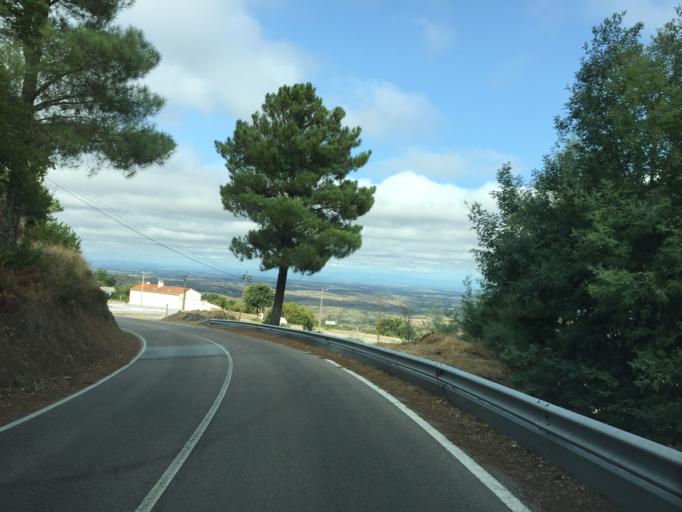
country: PT
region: Portalegre
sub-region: Marvao
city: Marvao
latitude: 39.4028
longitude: -7.3821
